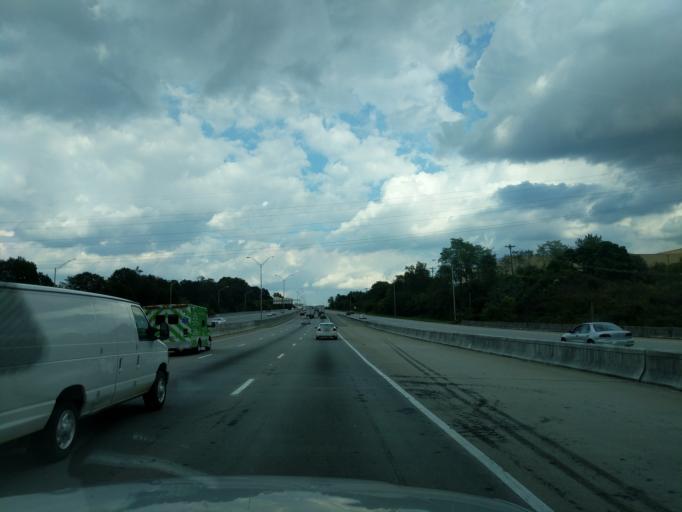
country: US
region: South Carolina
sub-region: Greenville County
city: Mauldin
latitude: 34.8009
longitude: -82.3650
